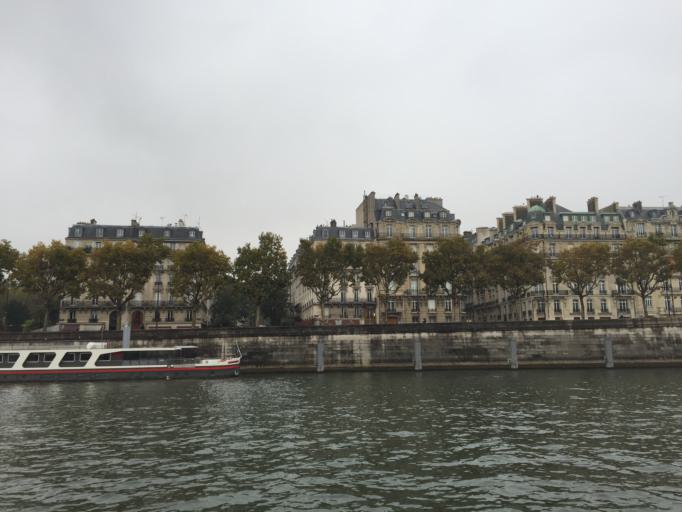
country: FR
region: Ile-de-France
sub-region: Departement des Hauts-de-Seine
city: Levallois-Perret
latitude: 48.8632
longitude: 2.2998
